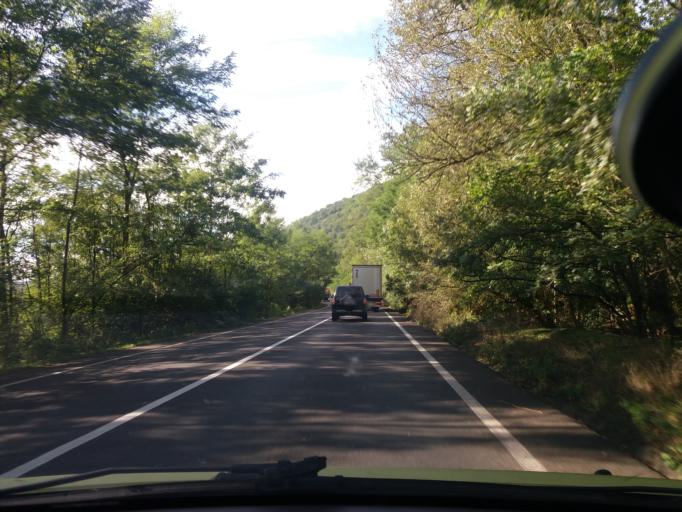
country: RO
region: Arad
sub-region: Comuna Savarsin
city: Savarsin
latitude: 46.0101
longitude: 22.2707
